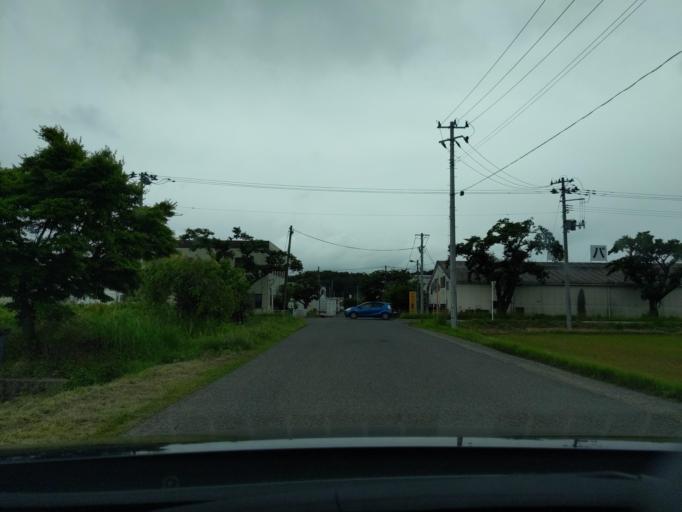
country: JP
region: Fukushima
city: Koriyama
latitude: 37.3625
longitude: 140.3438
